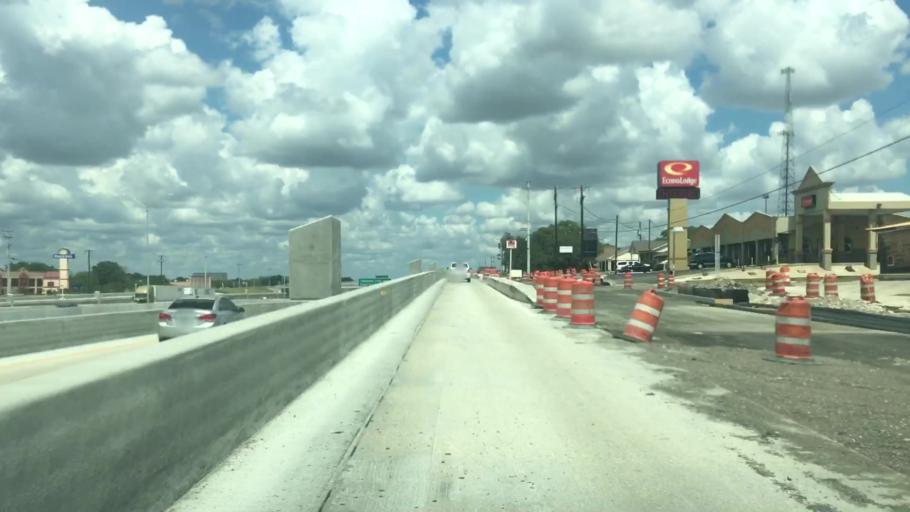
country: US
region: Texas
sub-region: Bell County
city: Temple
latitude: 31.1110
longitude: -97.3560
